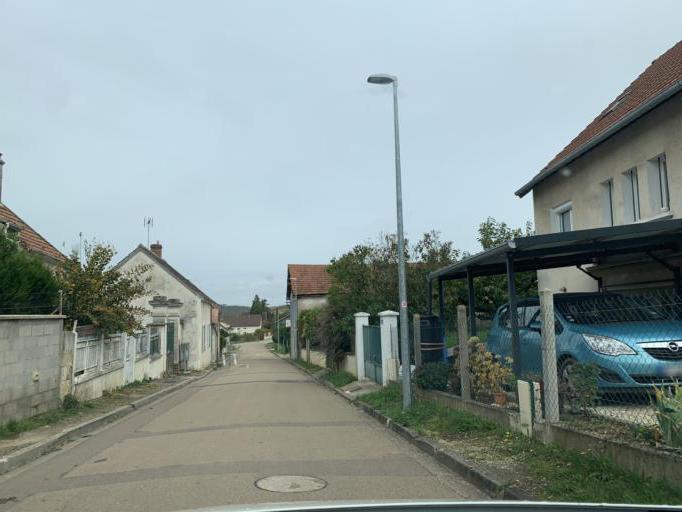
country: FR
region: Bourgogne
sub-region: Departement de l'Yonne
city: Champs-sur-Yonne
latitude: 47.7206
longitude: 3.5847
